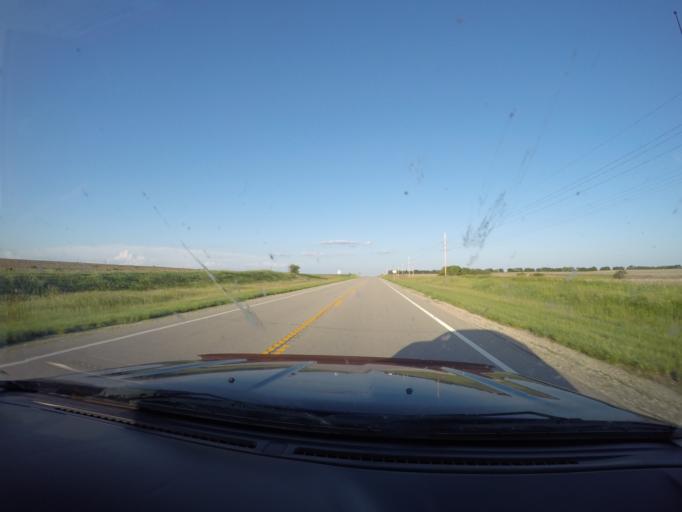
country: US
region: Kansas
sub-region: Washington County
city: Washington
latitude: 39.7114
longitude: -96.9727
